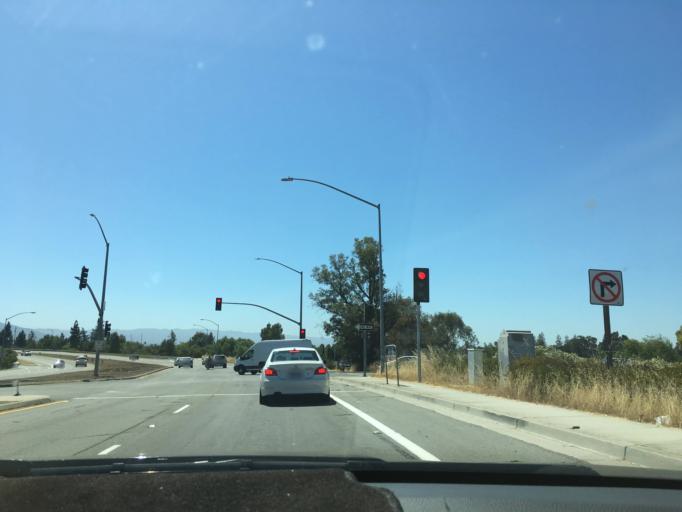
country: US
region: California
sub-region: Santa Clara County
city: Seven Trees
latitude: 37.2574
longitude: -121.7986
